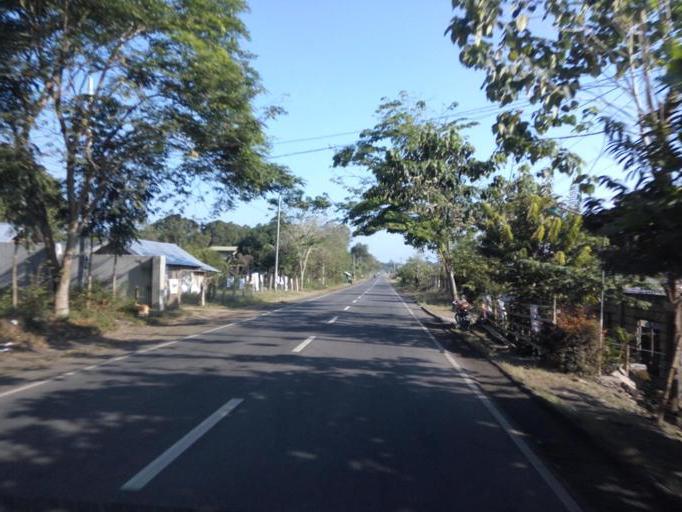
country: PH
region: Cagayan Valley
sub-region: Province of Cagayan
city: Minanga Norte
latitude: 17.7757
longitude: 121.7320
